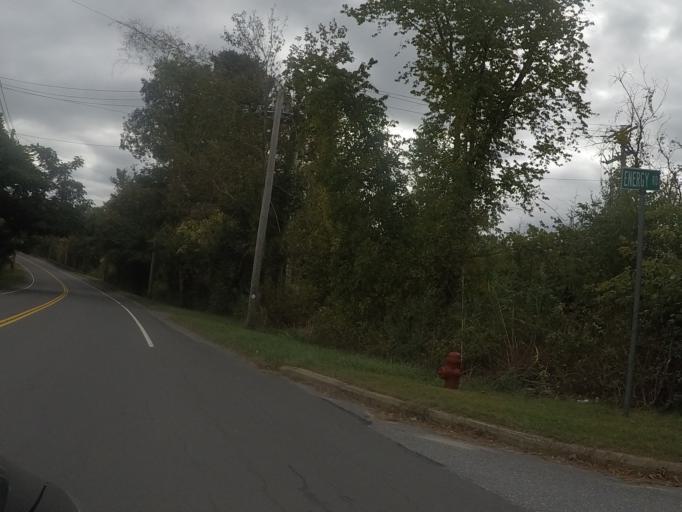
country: US
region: Massachusetts
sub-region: Bristol County
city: Smith Mills
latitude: 41.6783
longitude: -70.9985
